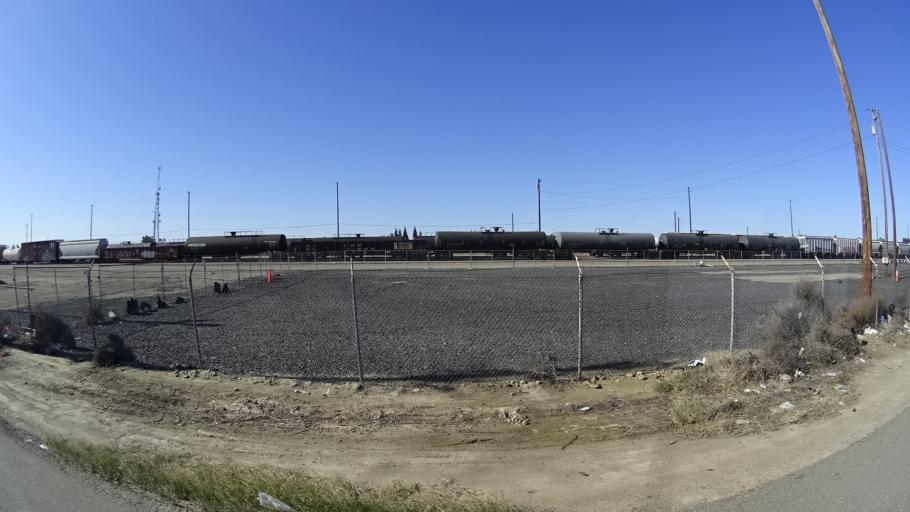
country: US
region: California
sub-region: Fresno County
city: West Park
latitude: 36.7884
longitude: -119.8523
